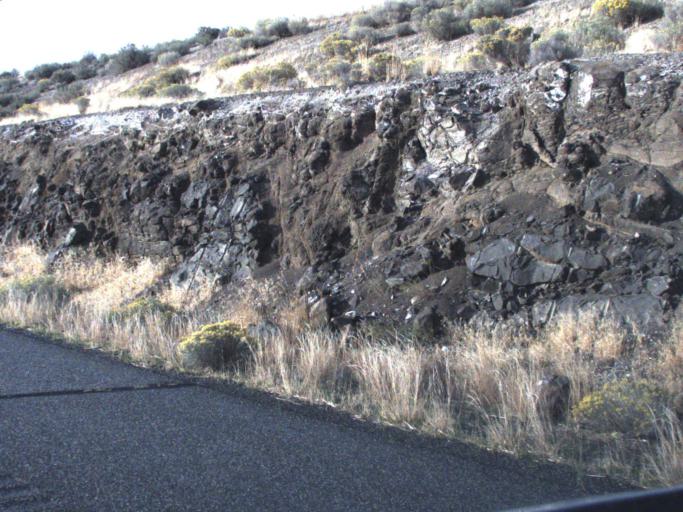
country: US
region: Washington
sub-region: Franklin County
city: West Pasco
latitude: 46.1848
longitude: -119.2487
